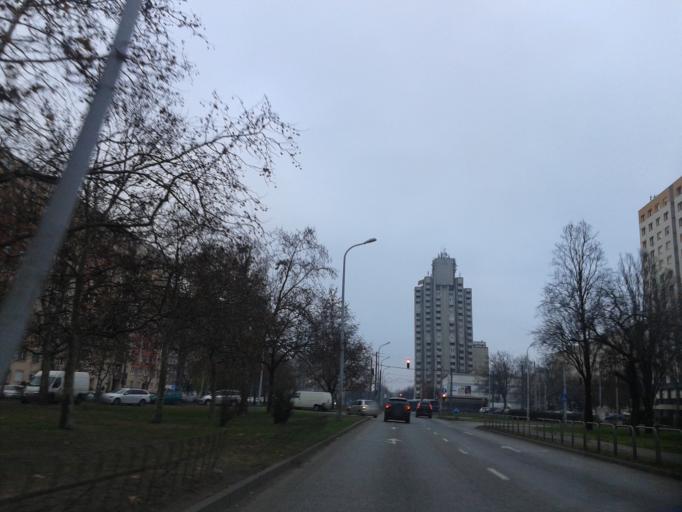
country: HU
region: Budapest
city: Budapest XV. keruelet
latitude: 47.5416
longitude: 19.1401
